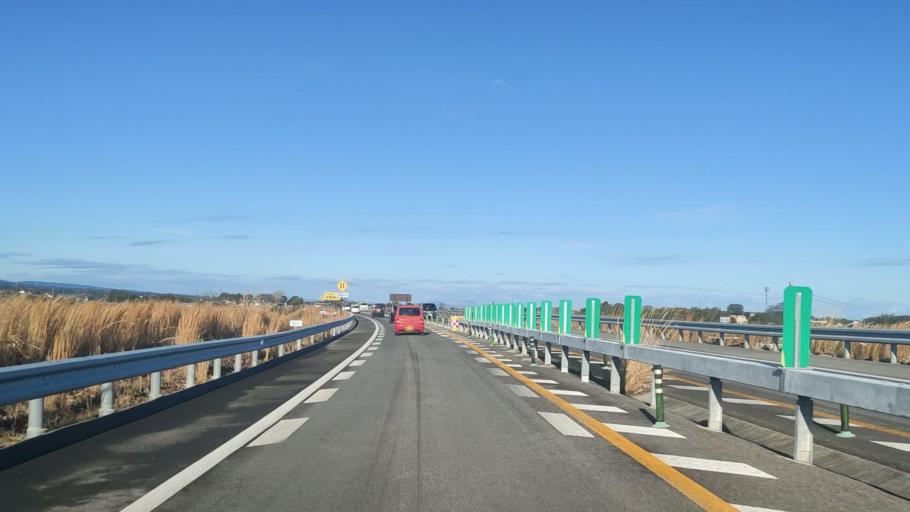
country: JP
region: Fukuoka
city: Nakatsu
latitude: 33.5420
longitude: 131.2147
